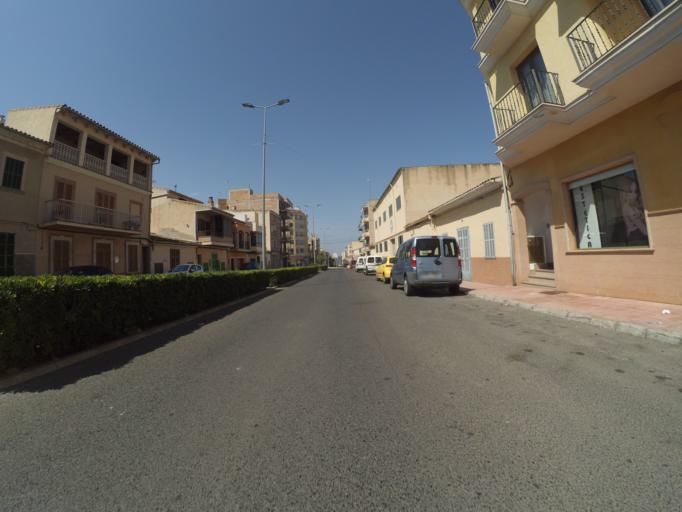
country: ES
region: Balearic Islands
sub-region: Illes Balears
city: Manacor
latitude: 39.5623
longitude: 3.2085
